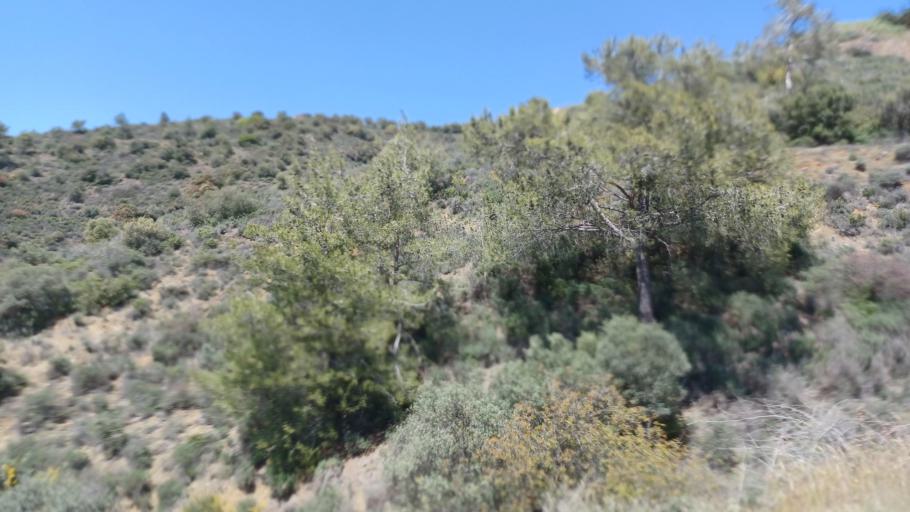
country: CY
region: Limassol
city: Parekklisha
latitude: 34.8198
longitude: 33.1450
